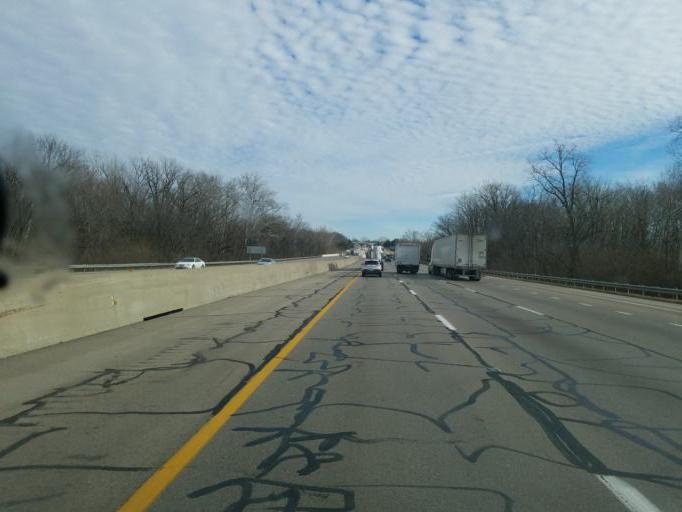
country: US
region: Ohio
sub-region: Montgomery County
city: Vandalia
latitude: 39.8663
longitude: -84.1711
